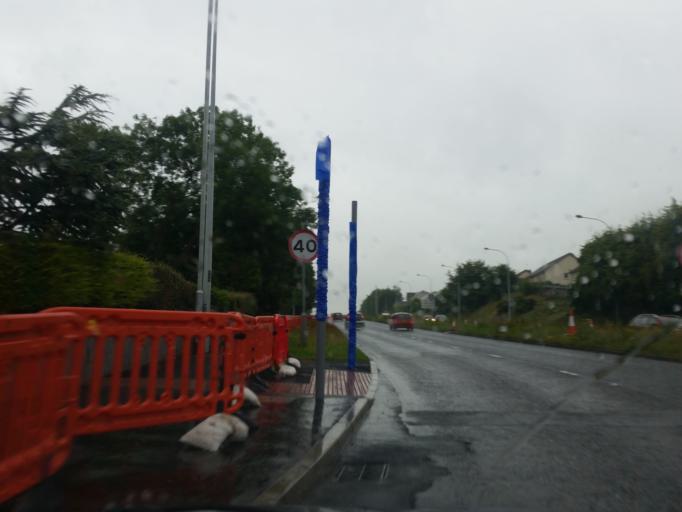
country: GB
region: Northern Ireland
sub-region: North Down District
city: Bangor
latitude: 54.6505
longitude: -5.6509
